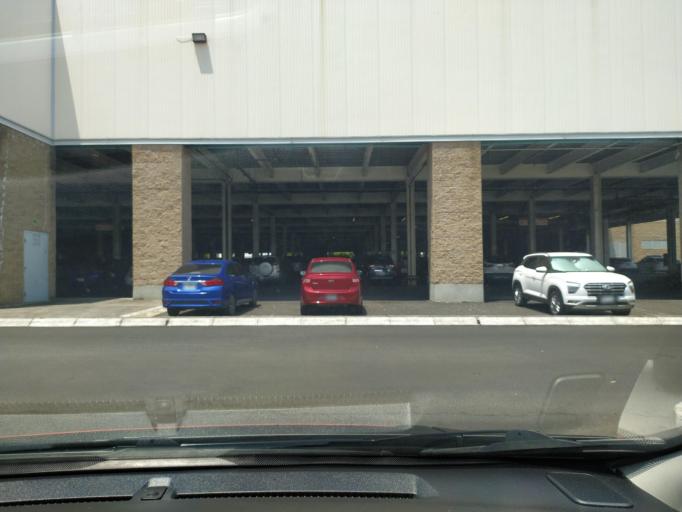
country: MX
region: Jalisco
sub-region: Tlajomulco de Zuniga
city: La Tijera
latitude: 20.5794
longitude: -103.4484
